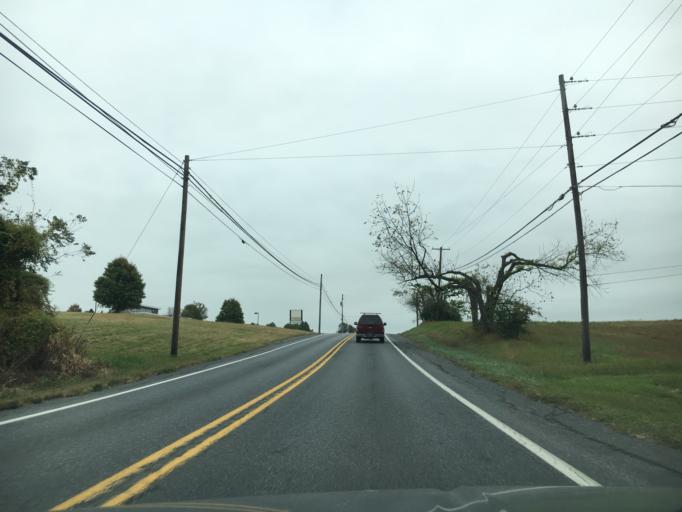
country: US
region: Pennsylvania
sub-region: Northampton County
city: Bath
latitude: 40.7033
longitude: -75.4230
